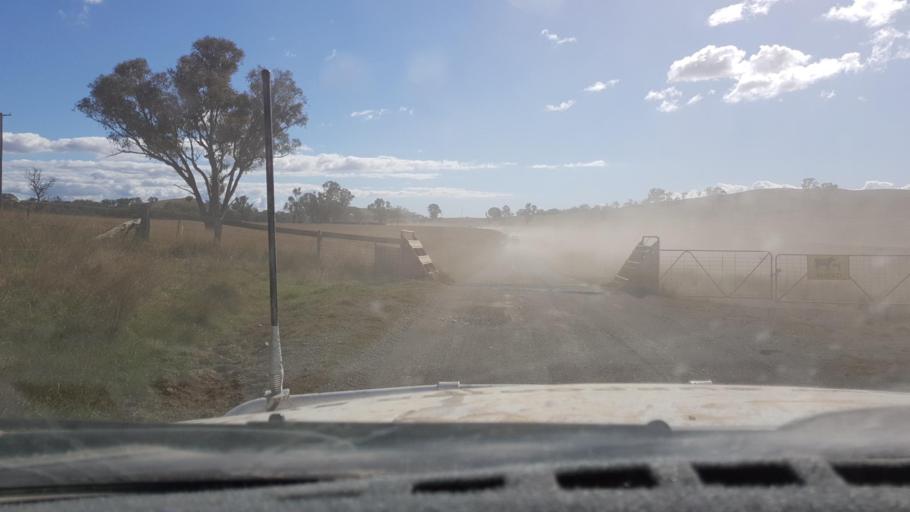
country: AU
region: New South Wales
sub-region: Narrabri
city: Blair Athol
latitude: -30.4936
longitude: 150.4412
